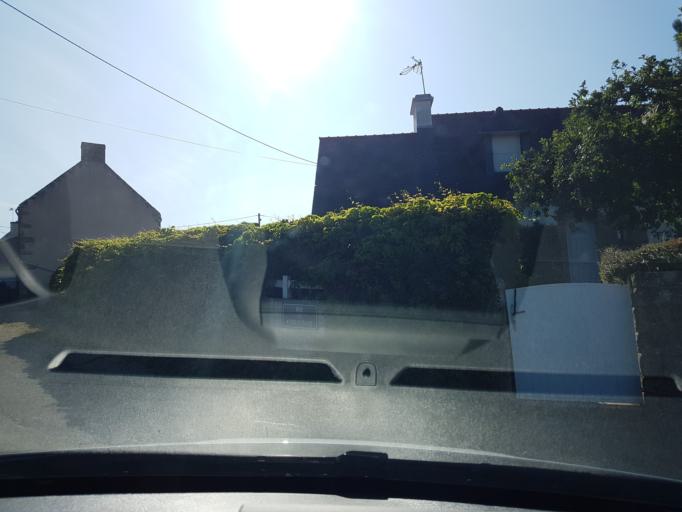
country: FR
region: Brittany
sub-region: Departement du Morbihan
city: Belz
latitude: 47.6806
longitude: -3.1878
